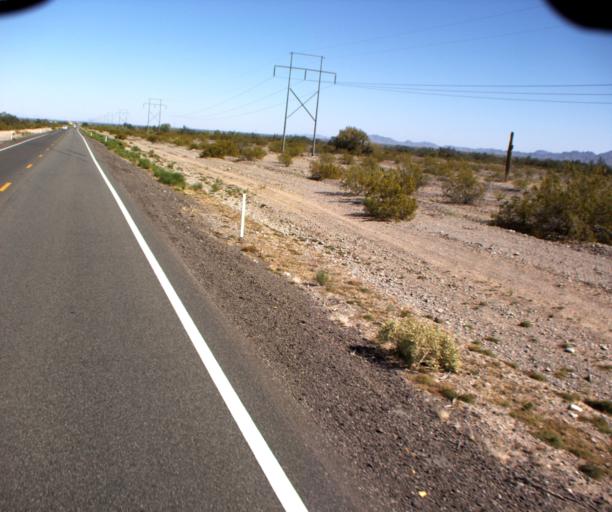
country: US
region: Arizona
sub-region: La Paz County
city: Quartzsite
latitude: 33.6354
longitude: -114.2171
